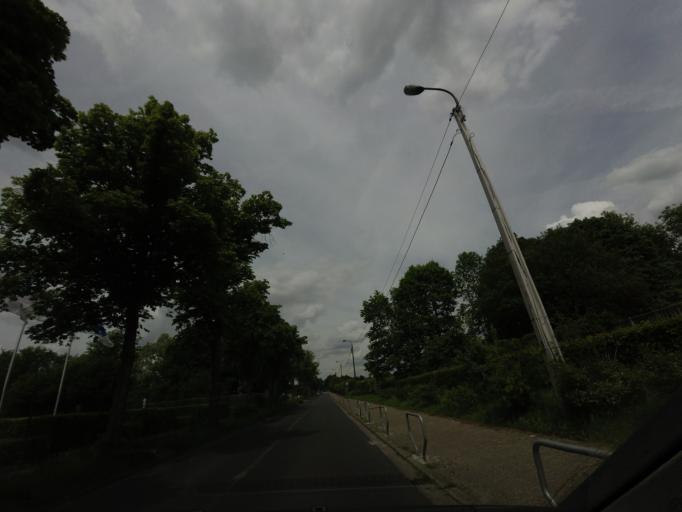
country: BE
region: Flanders
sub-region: Provincie Antwerpen
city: Bornem
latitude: 51.0964
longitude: 4.2679
